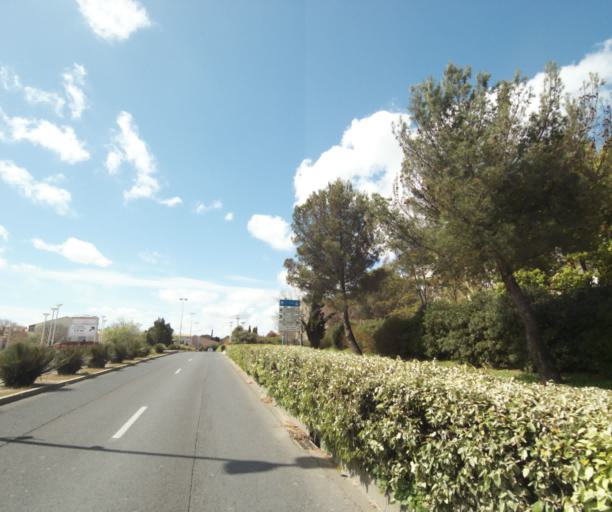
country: FR
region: Languedoc-Roussillon
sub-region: Departement de l'Herault
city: Lattes
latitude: 43.5708
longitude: 3.9042
